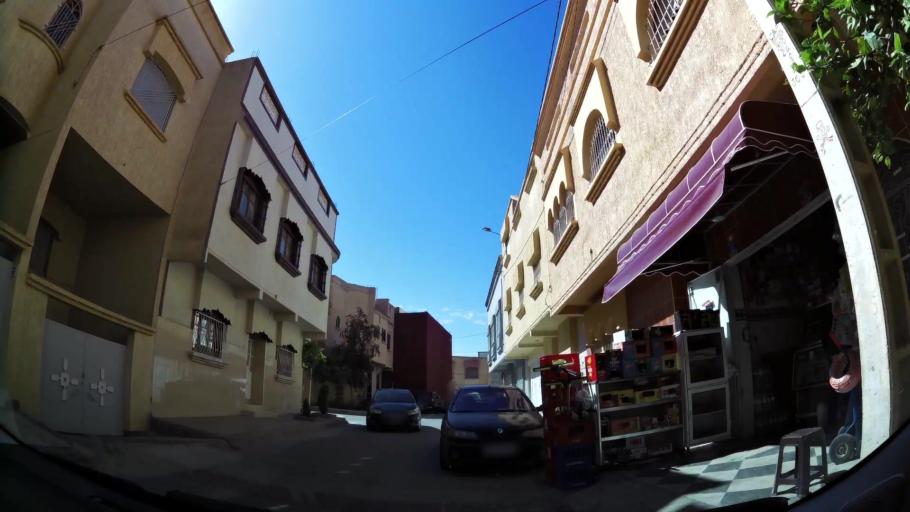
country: MA
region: Oriental
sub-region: Oujda-Angad
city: Oujda
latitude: 34.6560
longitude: -1.8901
